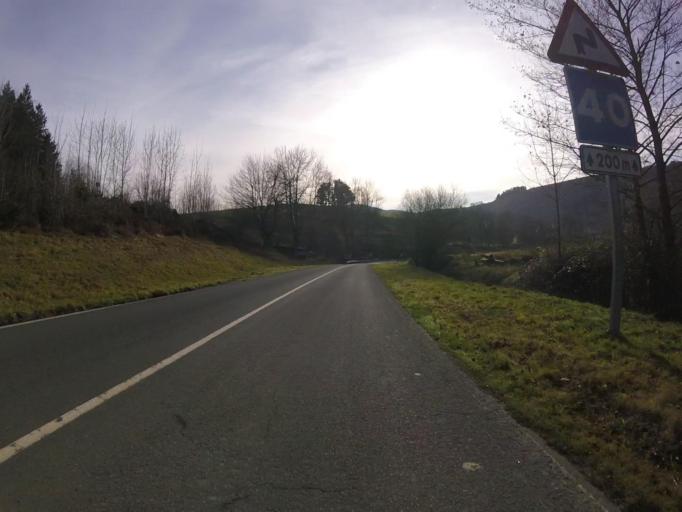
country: ES
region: Navarre
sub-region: Provincia de Navarra
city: Areso
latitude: 43.1015
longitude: -1.9528
